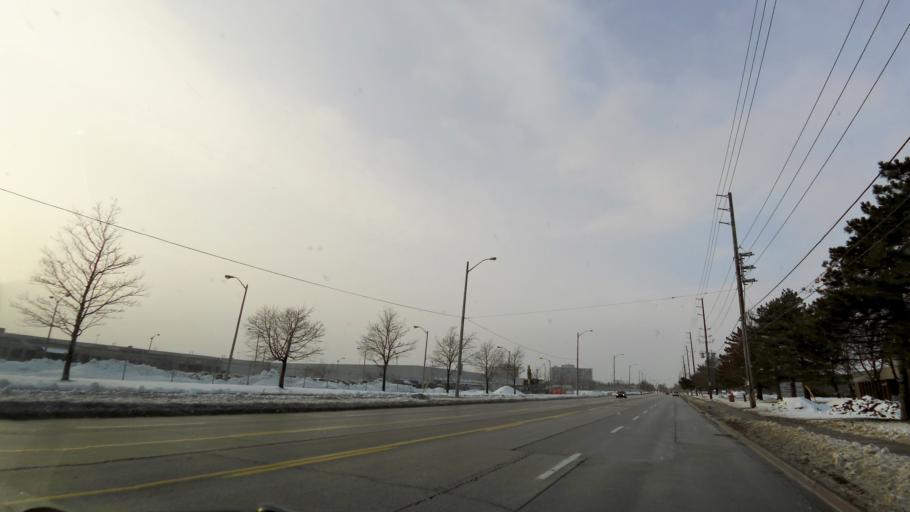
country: CA
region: Ontario
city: Brampton
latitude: 43.7050
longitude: -79.7284
